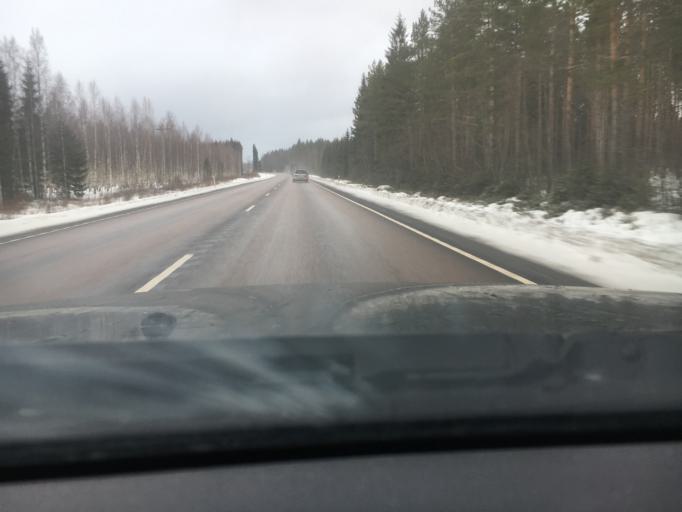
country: FI
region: Central Finland
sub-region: Joutsa
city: Leivonmaeki
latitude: 61.9328
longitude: 26.1147
